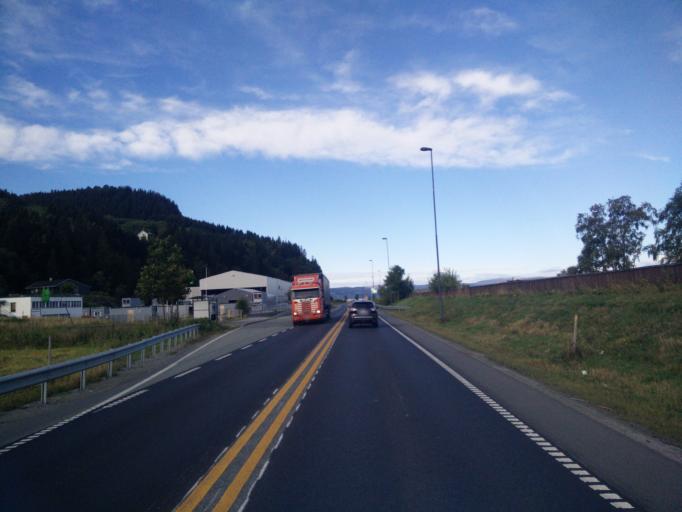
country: NO
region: Sor-Trondelag
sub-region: Melhus
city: Melhus
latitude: 63.3236
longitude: 10.2429
